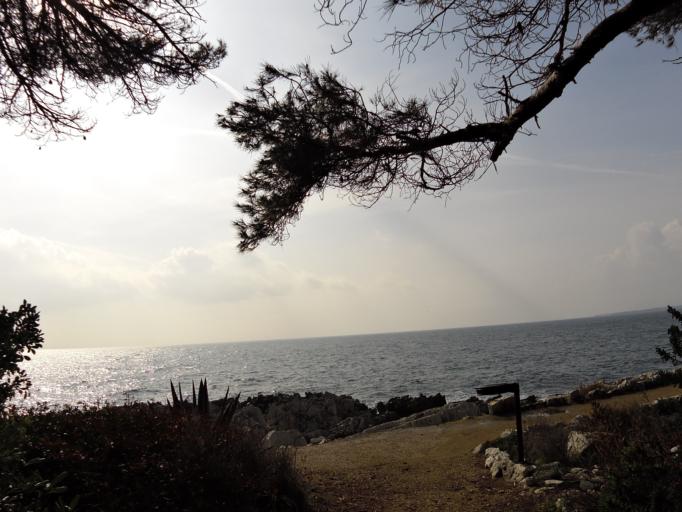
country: FR
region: Provence-Alpes-Cote d'Azur
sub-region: Departement des Alpes-Maritimes
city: Antibes
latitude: 43.5443
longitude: 7.1301
